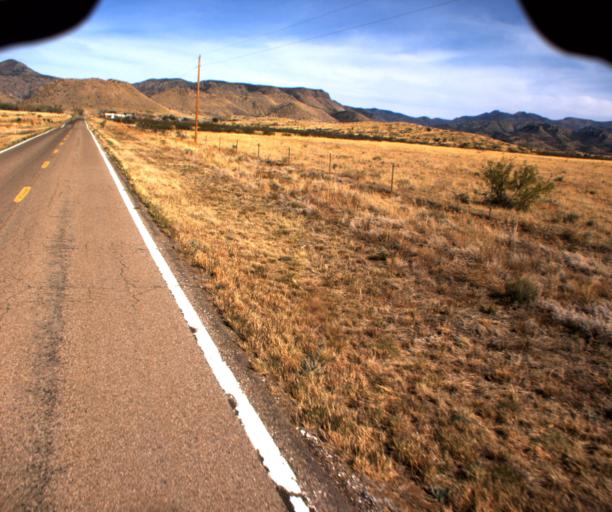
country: US
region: Arizona
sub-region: Cochise County
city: Willcox
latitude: 32.0067
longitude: -109.4133
